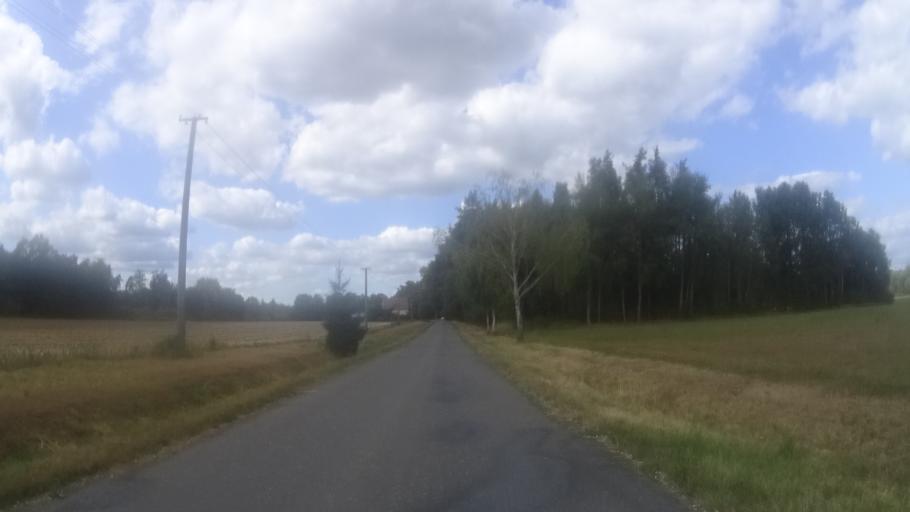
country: CZ
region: Pardubicky
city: Chocen
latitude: 50.0431
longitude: 16.1600
